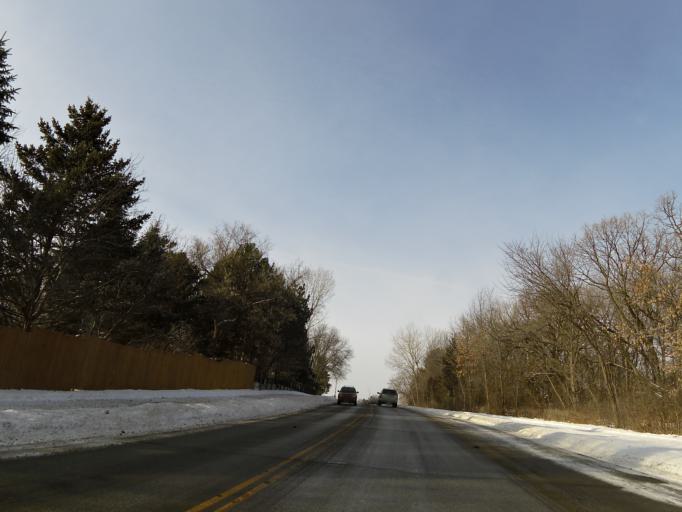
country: US
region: Minnesota
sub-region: Hennepin County
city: Eden Prairie
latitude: 44.8440
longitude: -93.4358
